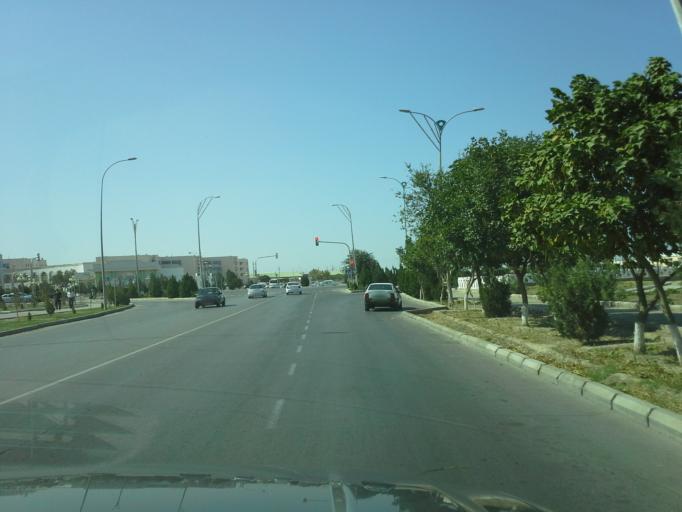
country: TM
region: Dasoguz
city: Dasoguz
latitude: 41.8449
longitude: 59.9333
